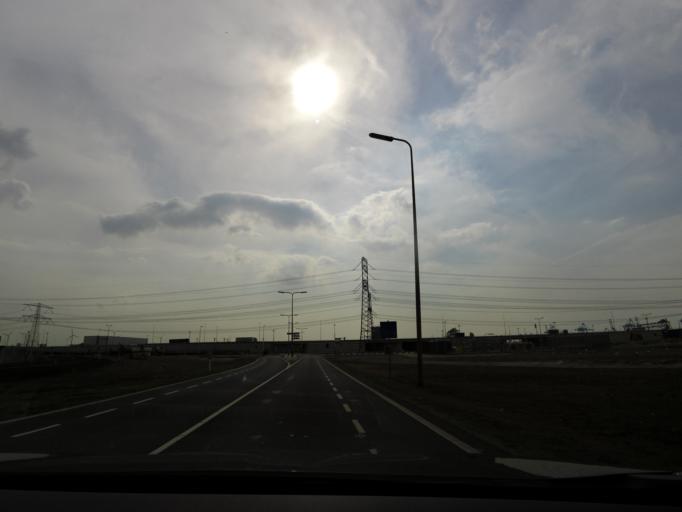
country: NL
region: South Holland
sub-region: Gemeente Rotterdam
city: Hoek van Holland
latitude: 51.9494
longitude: 4.0276
